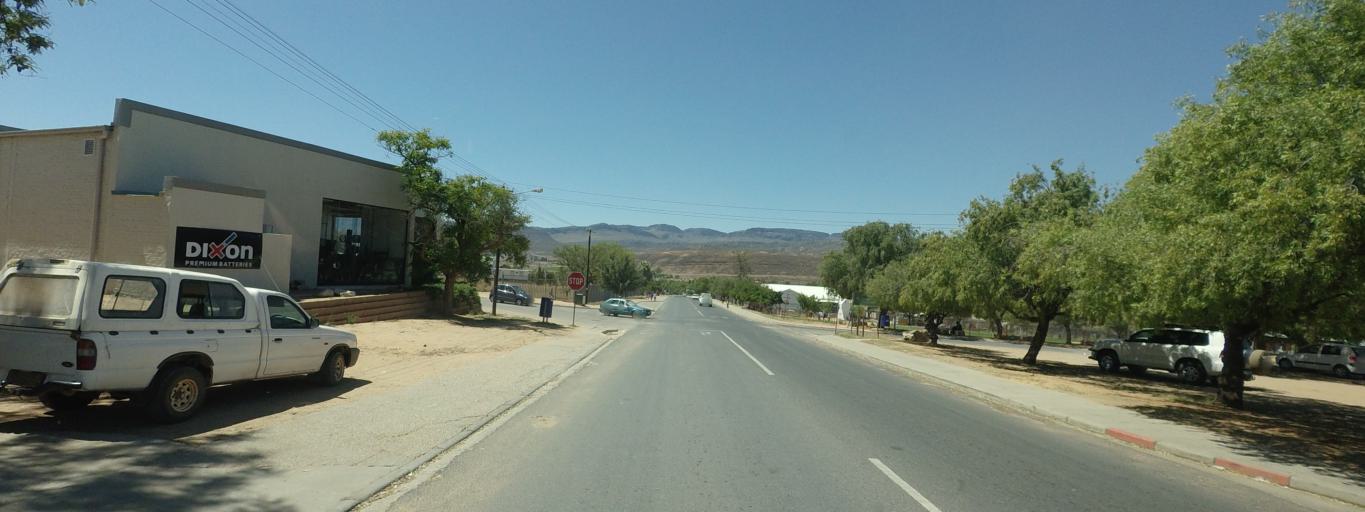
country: ZA
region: Western Cape
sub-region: West Coast District Municipality
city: Clanwilliam
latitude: -32.1858
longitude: 18.8910
